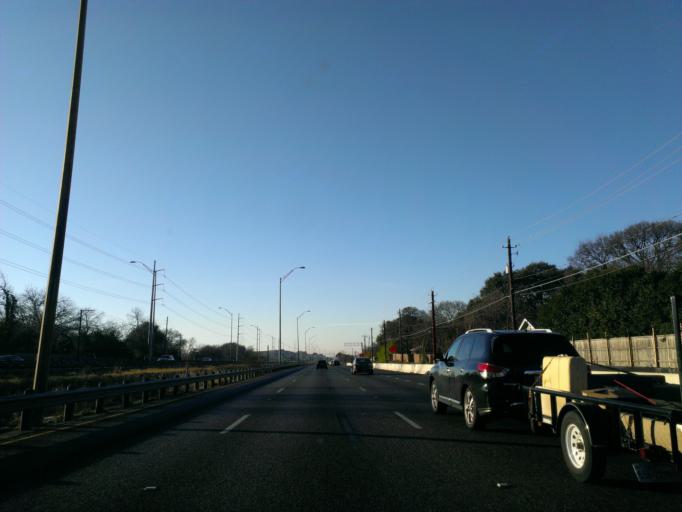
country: US
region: Texas
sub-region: Travis County
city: West Lake Hills
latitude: 30.3277
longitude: -97.7560
